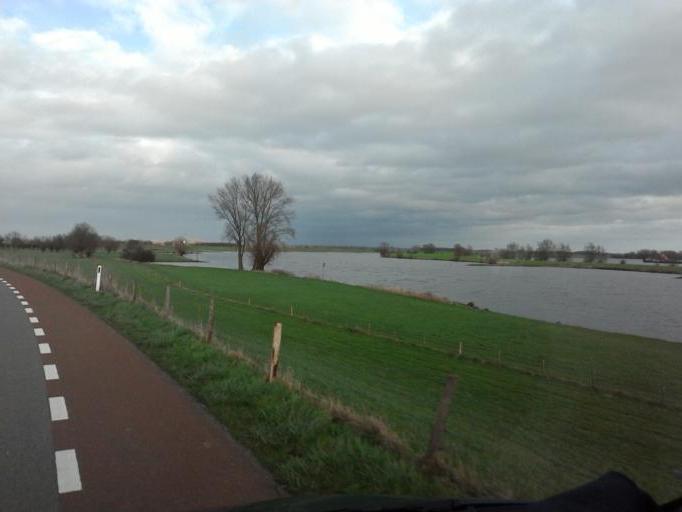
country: NL
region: Gelderland
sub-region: Gemeente Culemborg
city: Culemborg
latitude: 51.9738
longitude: 5.2259
